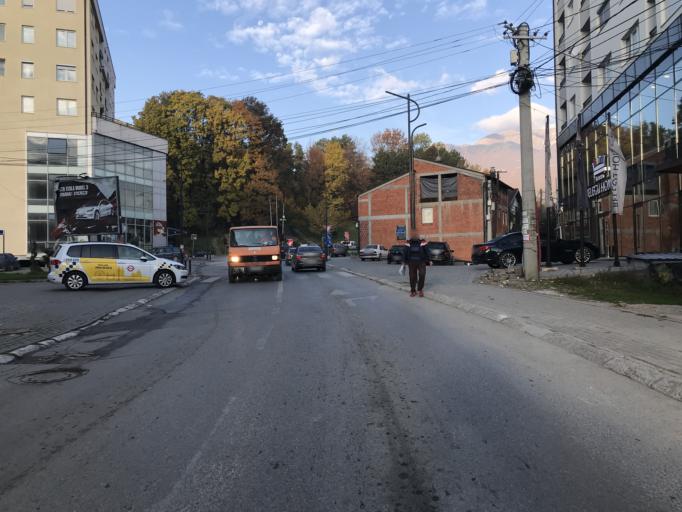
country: XK
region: Pec
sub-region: Komuna e Pejes
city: Peje
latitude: 42.6544
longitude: 20.2938
